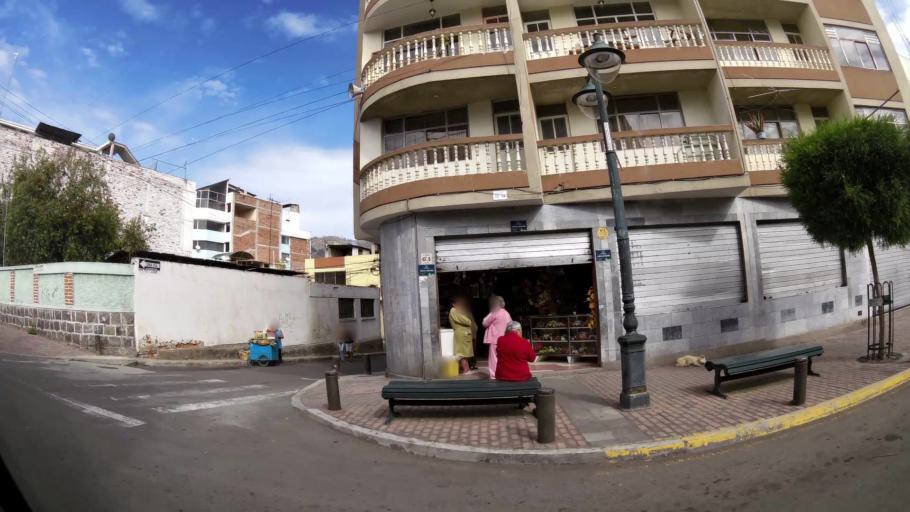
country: EC
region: Tungurahua
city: Ambato
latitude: -1.2441
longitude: -78.6360
